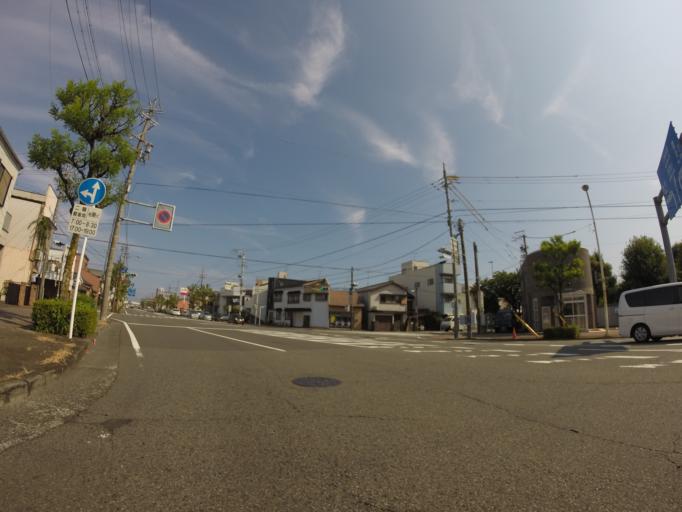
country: JP
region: Shizuoka
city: Shizuoka-shi
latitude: 34.9637
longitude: 138.3710
